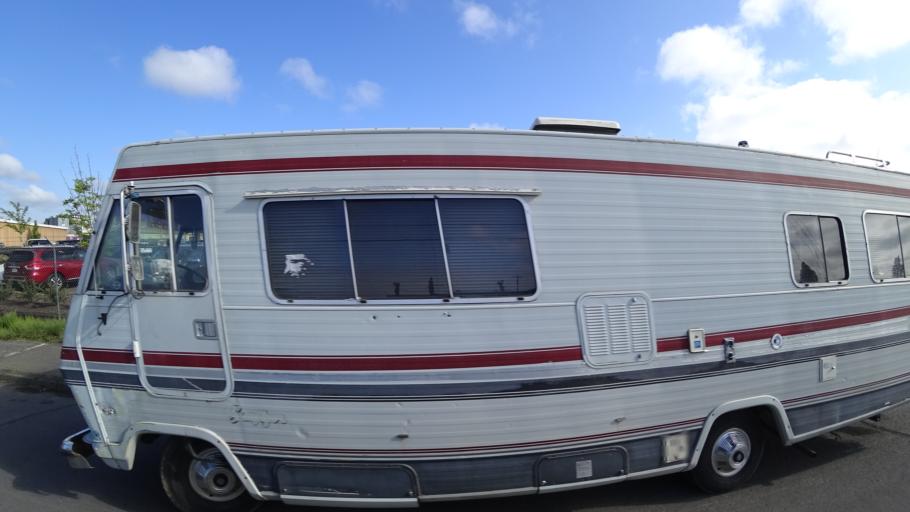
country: US
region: Oregon
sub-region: Washington County
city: Hillsboro
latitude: 45.5176
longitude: -122.9992
